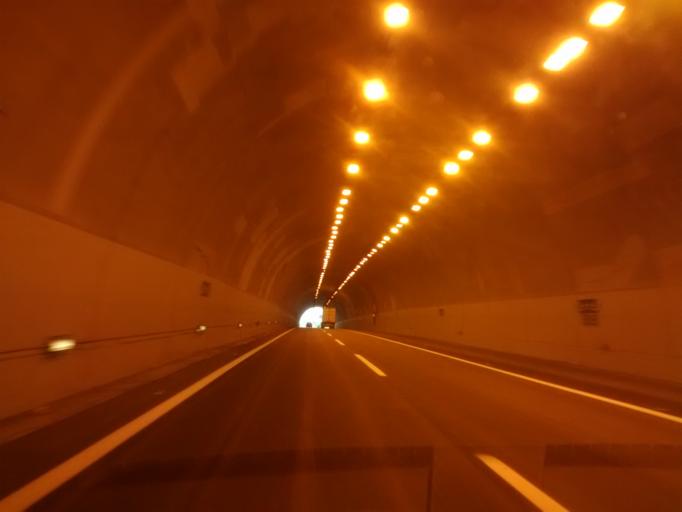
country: ES
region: Aragon
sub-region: Provincia de Zaragoza
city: Morata de Jalon
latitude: 41.4325
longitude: -1.4878
